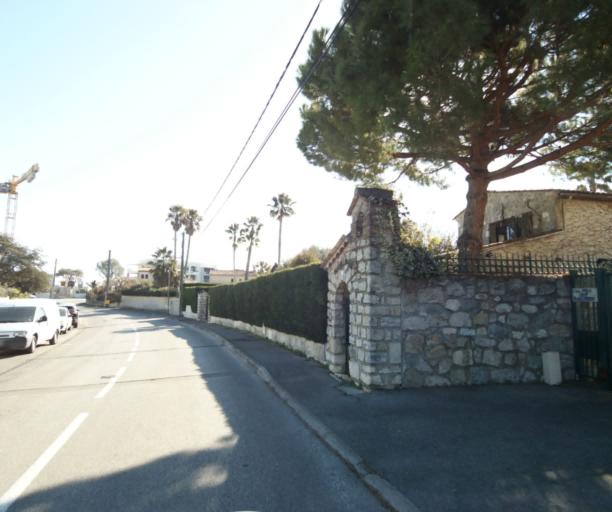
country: FR
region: Provence-Alpes-Cote d'Azur
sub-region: Departement des Alpes-Maritimes
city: Biot
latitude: 43.5988
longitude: 7.1043
